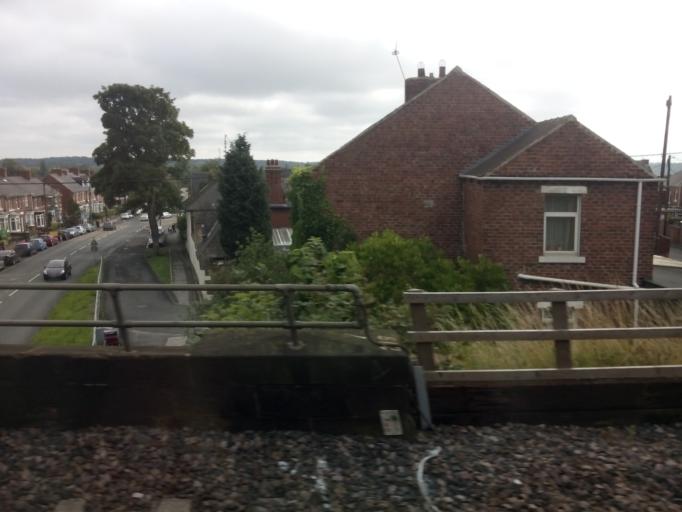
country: GB
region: England
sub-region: County Durham
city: Chester-le-Street
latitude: 54.8526
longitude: -1.5769
